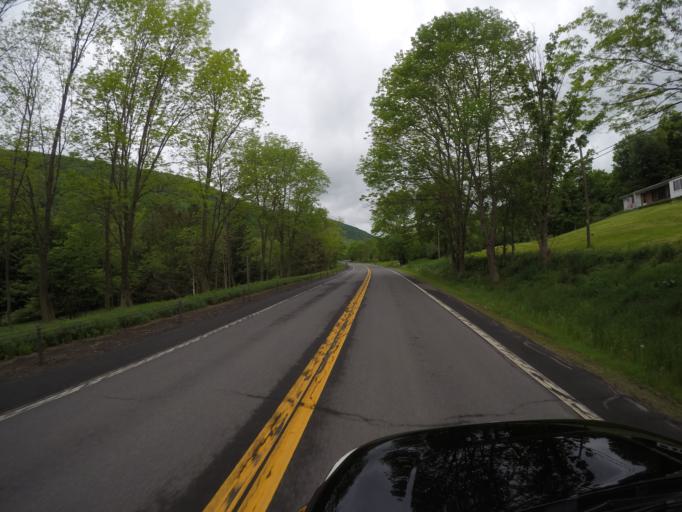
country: US
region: New York
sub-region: Delaware County
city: Delhi
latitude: 42.2501
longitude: -74.8370
